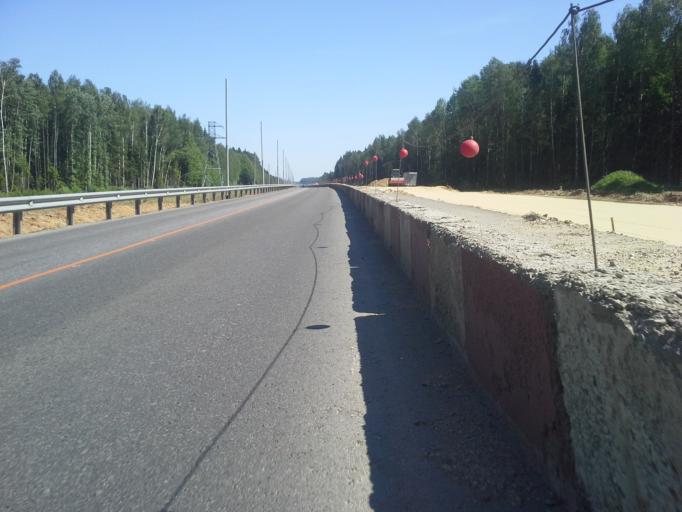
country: RU
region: Moskovskaya
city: Aprelevka
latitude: 55.4681
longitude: 37.0835
